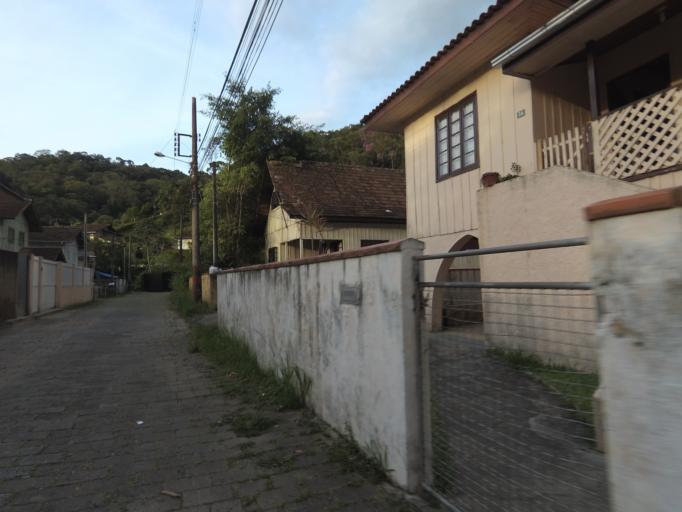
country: BR
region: Santa Catarina
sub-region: Blumenau
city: Blumenau
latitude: -26.9278
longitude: -49.0471
